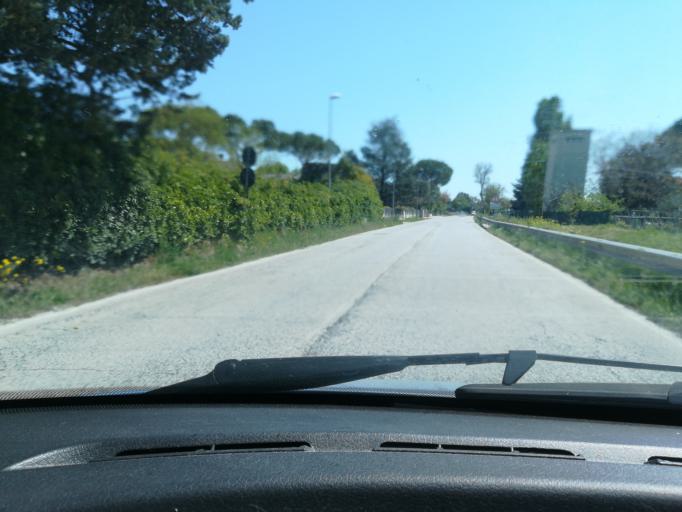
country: IT
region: The Marches
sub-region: Provincia di Ancona
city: Castelfidardo
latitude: 43.4543
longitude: 13.5246
